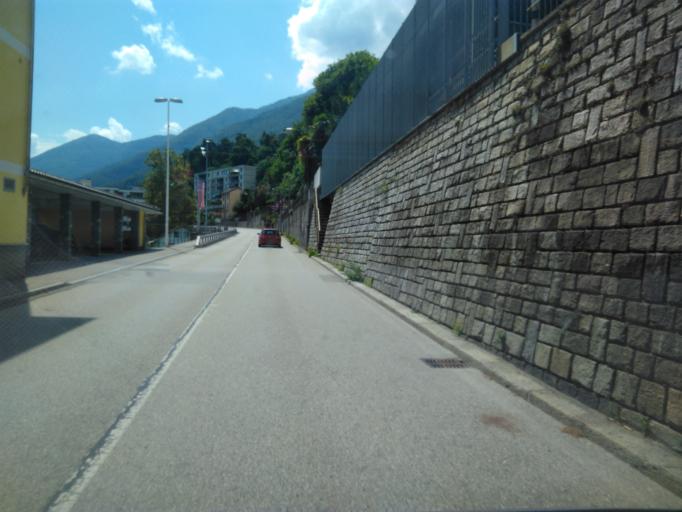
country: CH
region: Ticino
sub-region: Locarno District
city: Brissago
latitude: 46.1236
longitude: 8.7144
